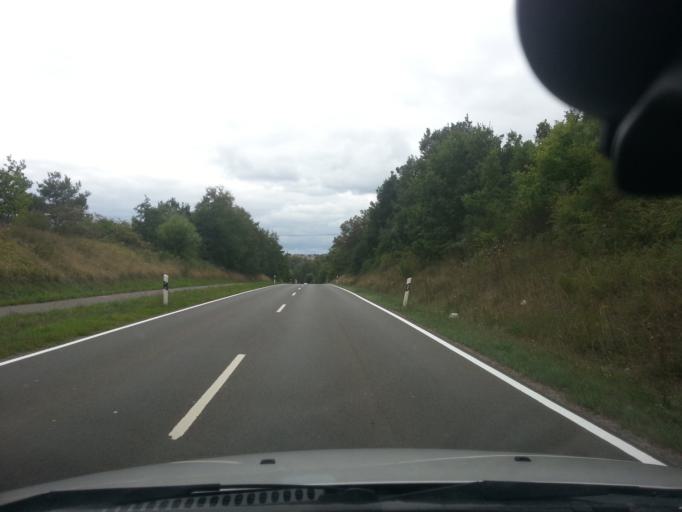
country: DE
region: Rheinland-Pfalz
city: Eisenberg
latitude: 49.5490
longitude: 8.0728
